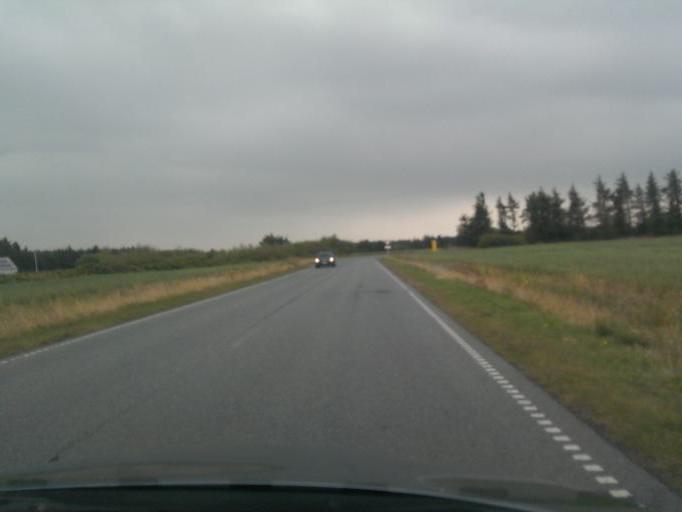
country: DK
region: North Denmark
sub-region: Jammerbugt Kommune
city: Pandrup
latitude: 57.3672
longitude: 9.7295
